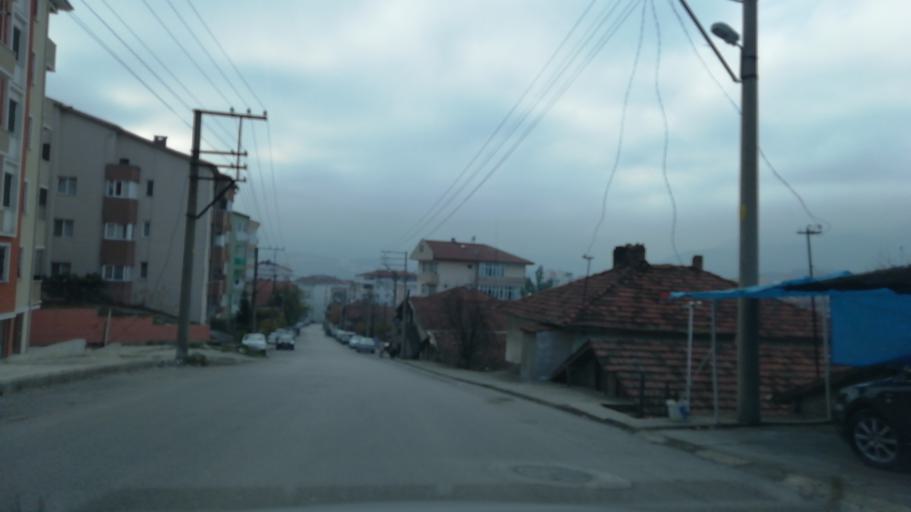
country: TR
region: Karabuk
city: Karabuk
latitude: 41.2103
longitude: 32.6279
